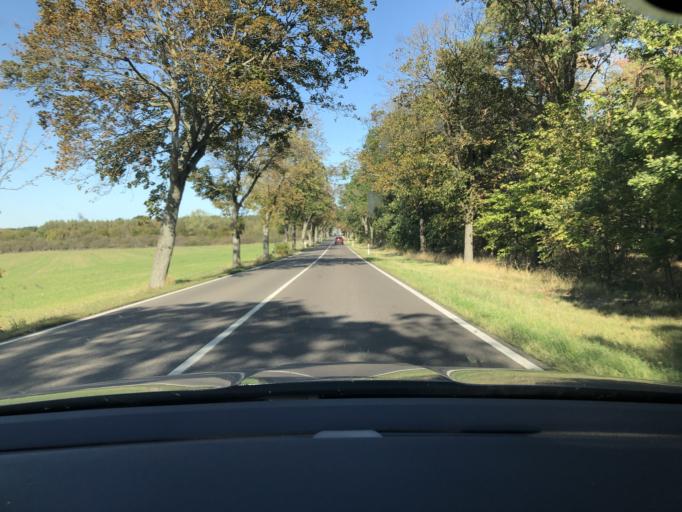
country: DE
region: Saxony-Anhalt
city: Kropstadt
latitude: 51.9769
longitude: 12.7598
